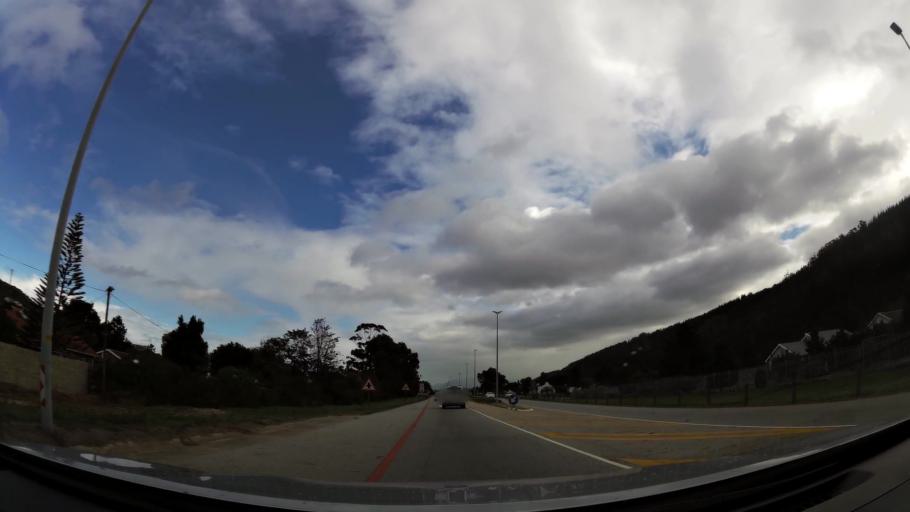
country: ZA
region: Western Cape
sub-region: Eden District Municipality
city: Knysna
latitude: -34.0191
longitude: 22.8171
